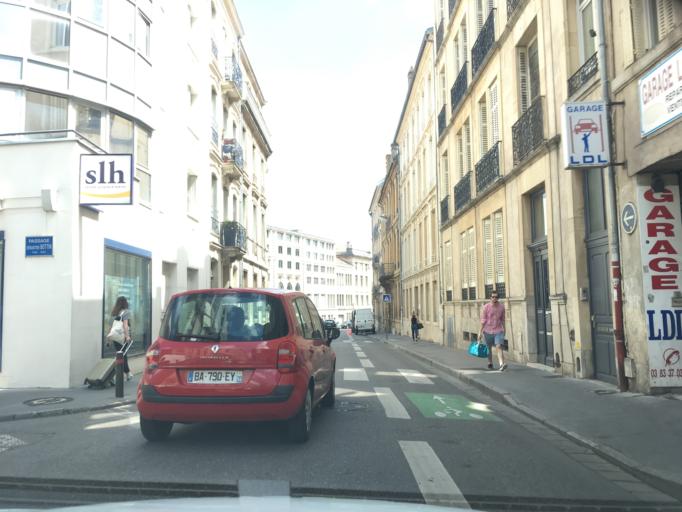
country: FR
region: Lorraine
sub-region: Departement de Meurthe-et-Moselle
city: Nancy
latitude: 48.6917
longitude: 6.1758
